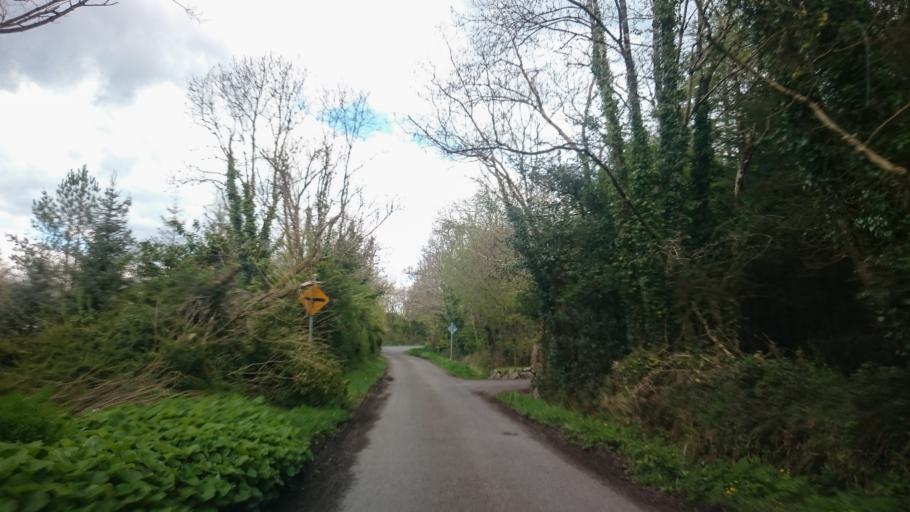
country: IE
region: Munster
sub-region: Waterford
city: Waterford
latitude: 52.2340
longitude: -7.0334
